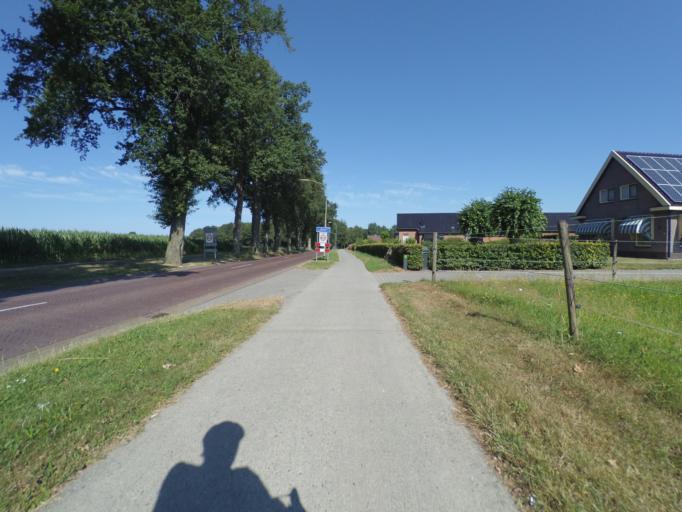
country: NL
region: Drenthe
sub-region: Gemeente Borger-Odoorn
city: Borger
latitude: 52.9115
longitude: 6.8014
